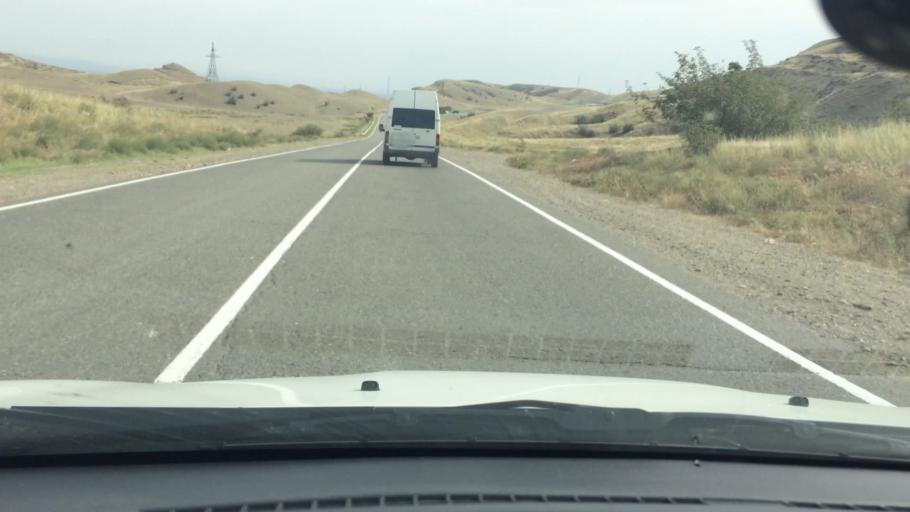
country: GE
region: Kvemo Kartli
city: Rust'avi
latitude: 41.5354
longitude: 44.9794
